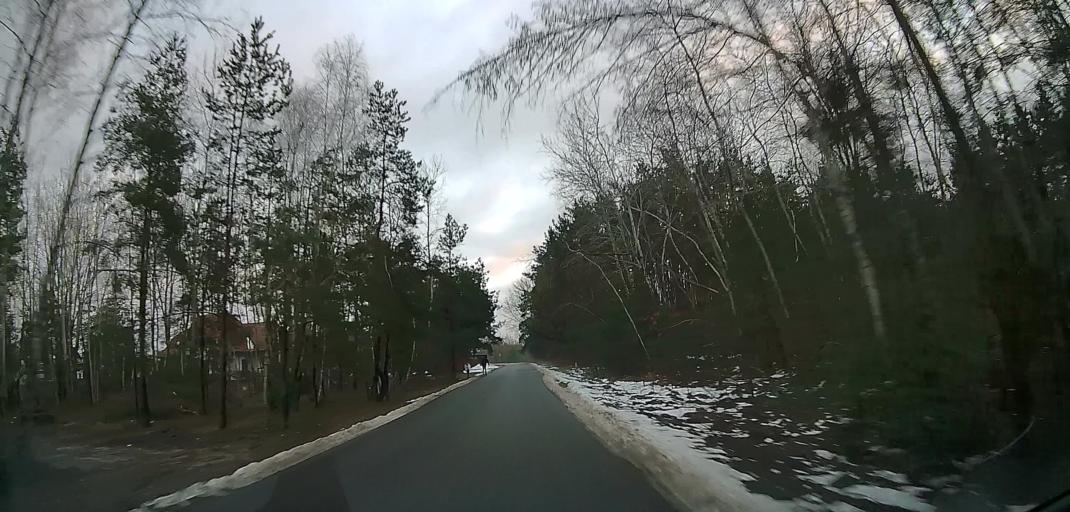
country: PL
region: Masovian Voivodeship
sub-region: Radom
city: Radom
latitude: 51.4518
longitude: 21.1309
